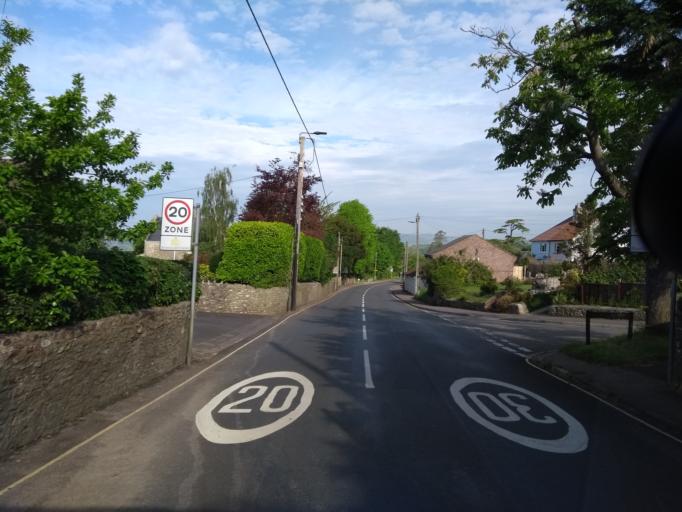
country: GB
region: England
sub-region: Devon
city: Axminster
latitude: 50.7803
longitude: -2.9913
